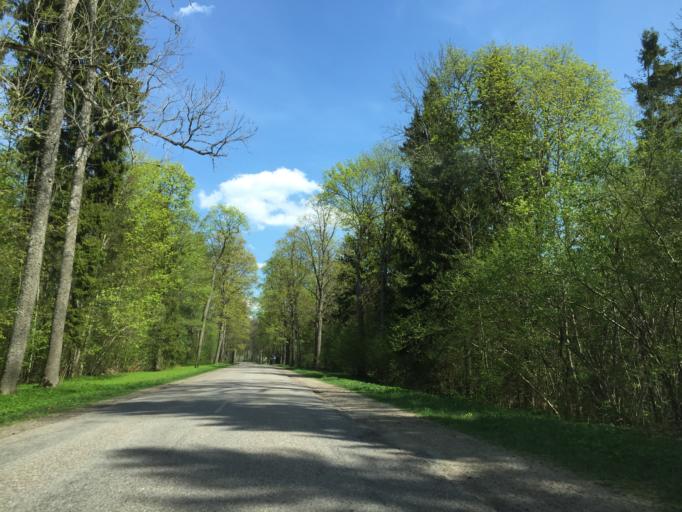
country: LV
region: Krimulda
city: Ragana
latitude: 57.3389
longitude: 24.6535
